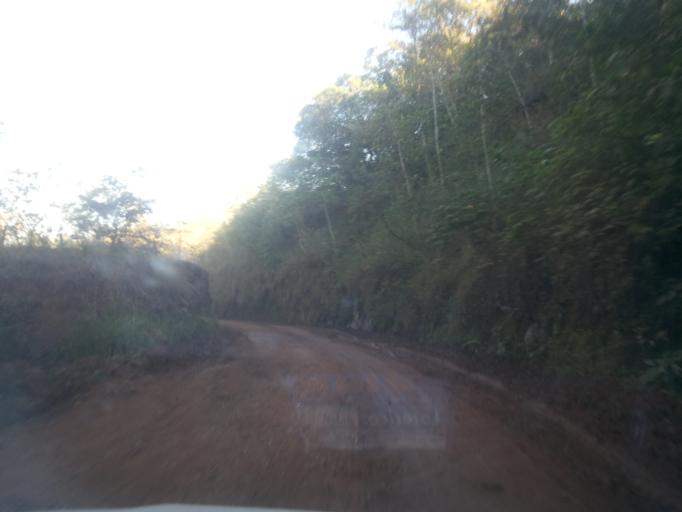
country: BR
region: Minas Gerais
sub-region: Campina Verde
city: Campina Verde
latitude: -19.3167
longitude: -49.8112
